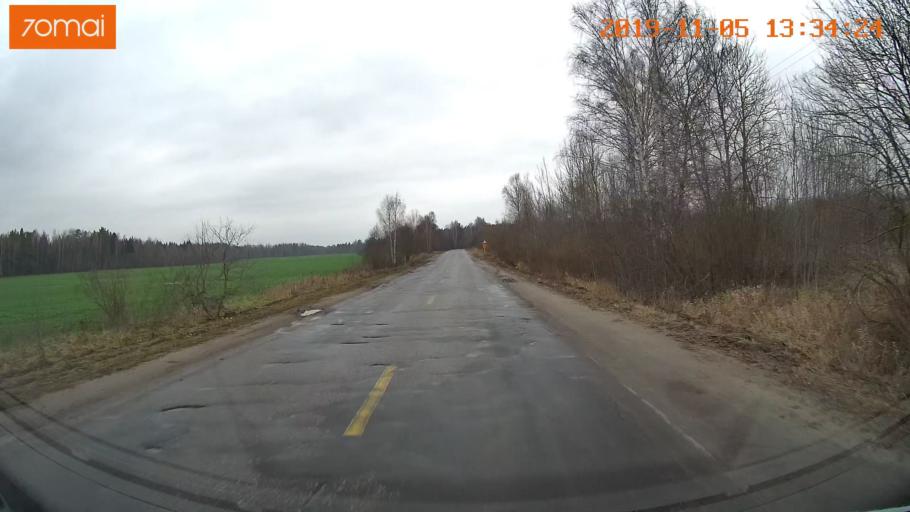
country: RU
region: Ivanovo
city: Shuya
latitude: 56.9003
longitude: 41.3900
